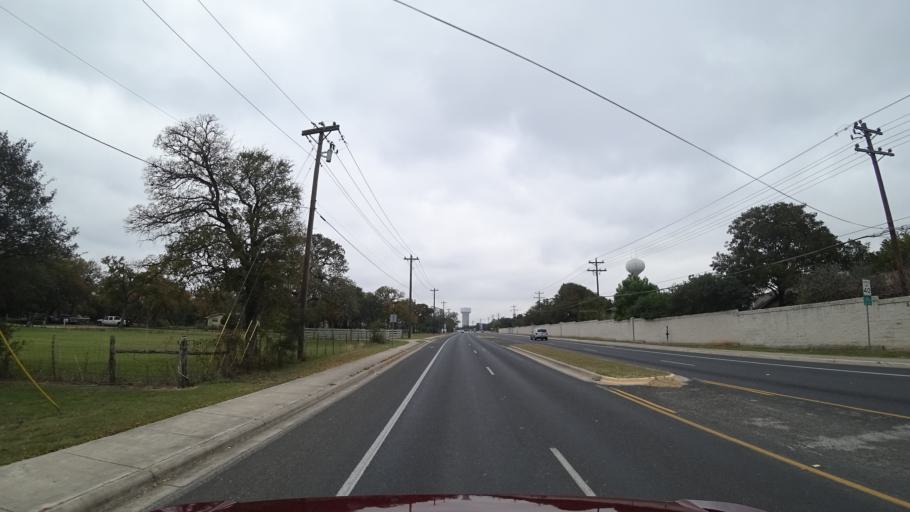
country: US
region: Texas
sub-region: Williamson County
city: Anderson Mill
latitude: 30.4527
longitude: -97.8225
